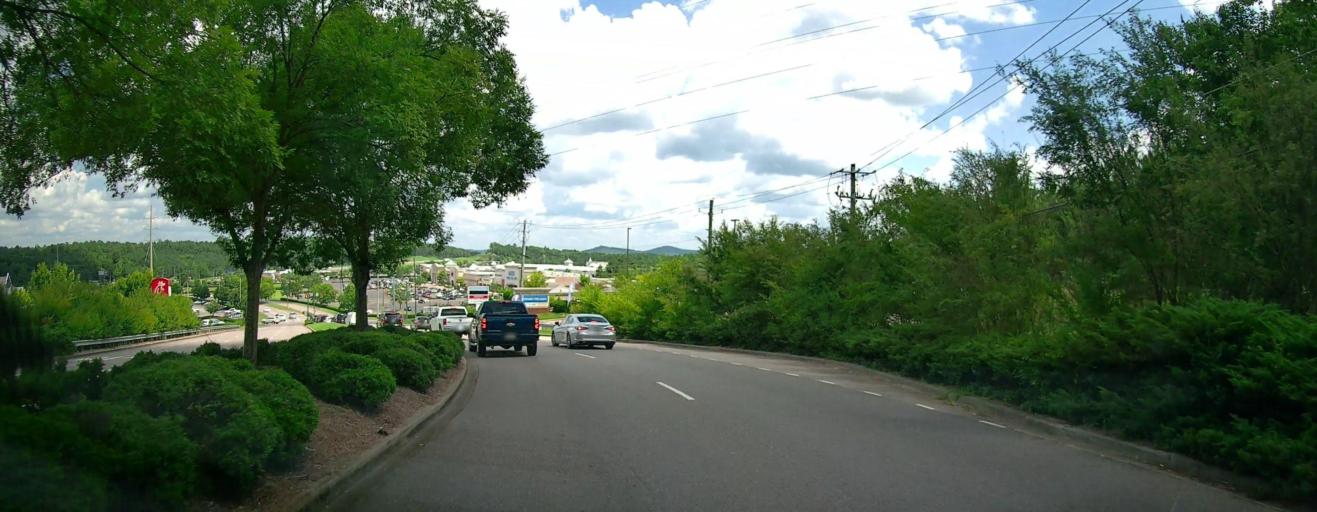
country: US
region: Alabama
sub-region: Shelby County
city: Alabaster
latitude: 33.2286
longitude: -86.8032
